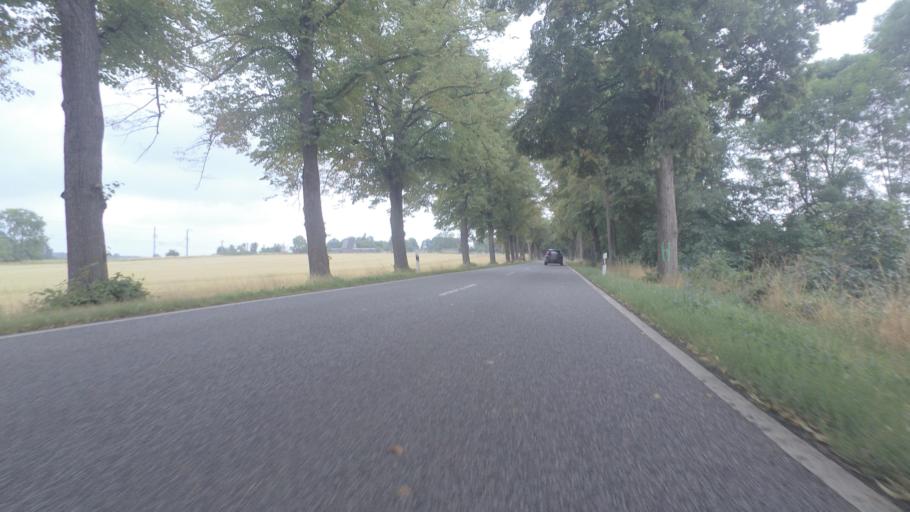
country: DE
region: Brandenburg
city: Wustermark
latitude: 52.5135
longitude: 12.9690
